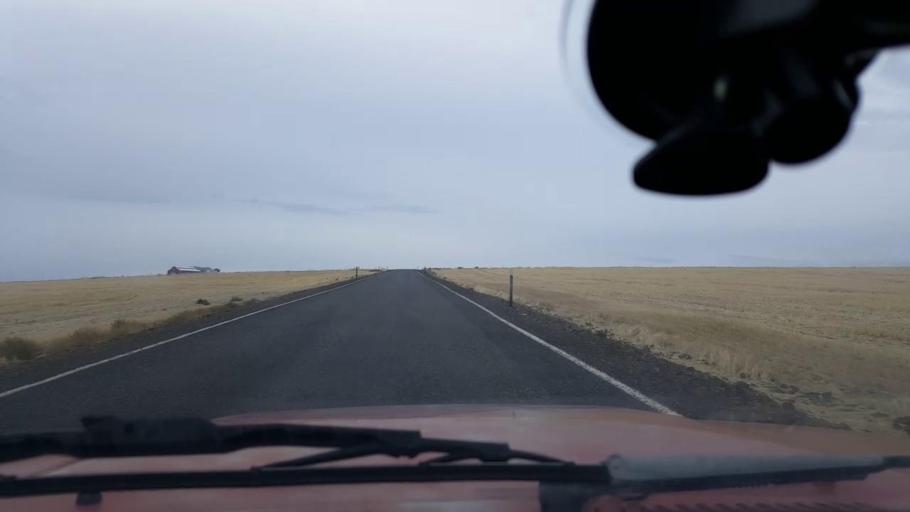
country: US
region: Washington
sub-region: Asotin County
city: Clarkston Heights-Vineland
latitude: 46.3417
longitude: -117.2693
